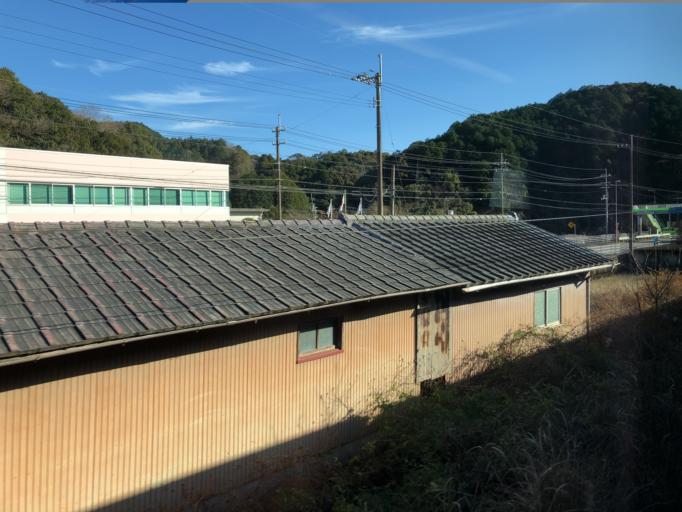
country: JP
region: Kochi
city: Nakamura
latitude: 33.1063
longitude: 133.0986
